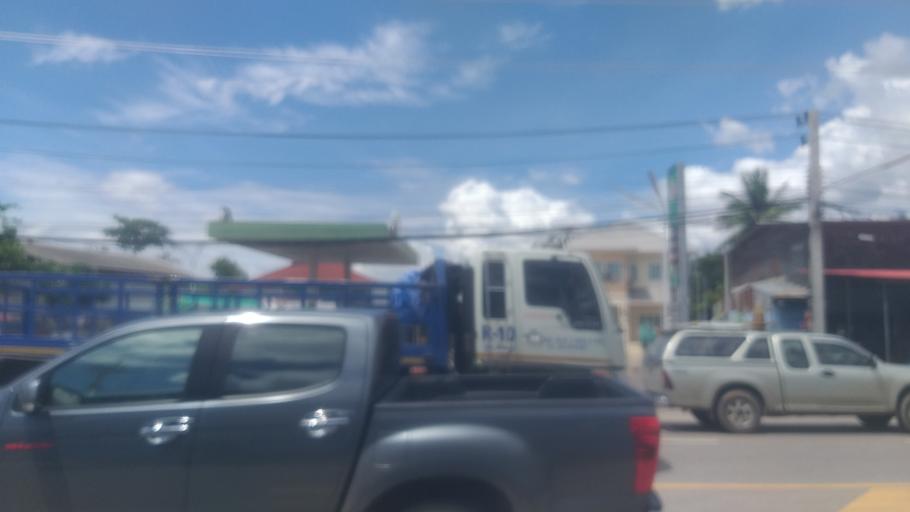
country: TH
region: Nakhon Ratchasima
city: Phra Thong Kham
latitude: 15.2685
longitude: 102.0194
